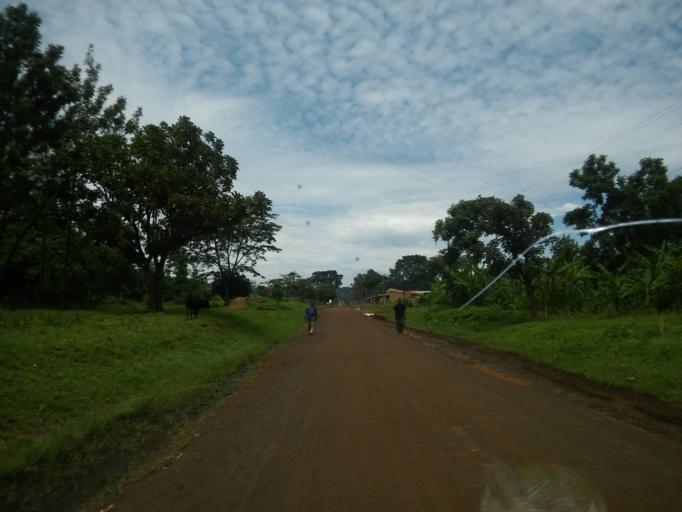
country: UG
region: Eastern Region
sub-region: Tororo District
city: Tororo
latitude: 0.8278
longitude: 34.2891
